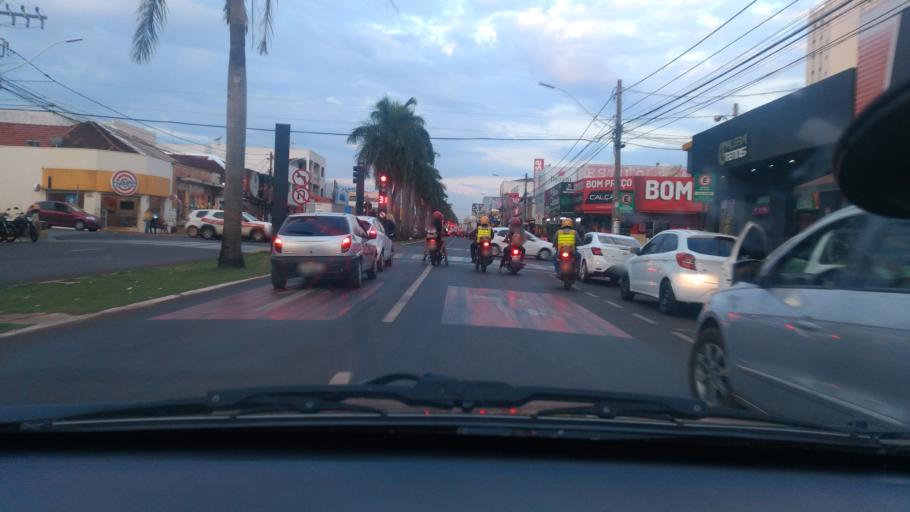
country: BR
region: Goias
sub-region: Santa Helena De Goias
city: Santa Helena de Goias
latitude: -17.7933
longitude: -50.9283
